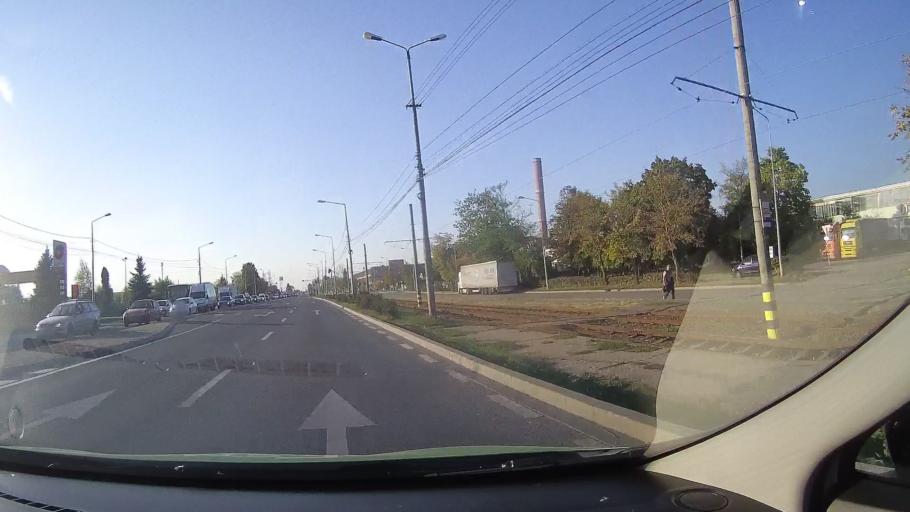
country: RO
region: Bihor
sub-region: Comuna Biharea
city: Oradea
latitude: 47.0786
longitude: 21.8979
